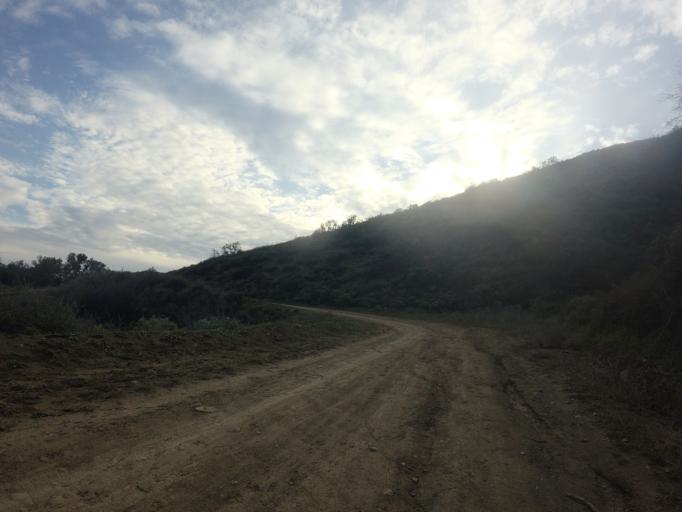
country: US
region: California
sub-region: Riverside County
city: Corona
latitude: 33.8035
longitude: -117.6548
